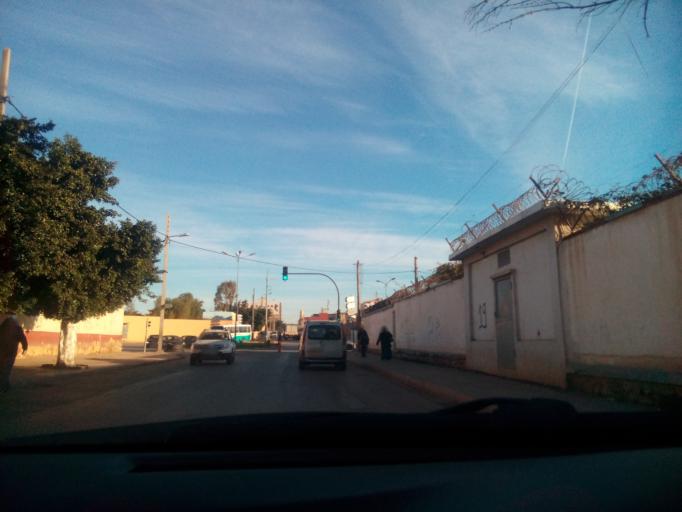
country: DZ
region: Oran
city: Oran
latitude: 35.6754
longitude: -0.6624
